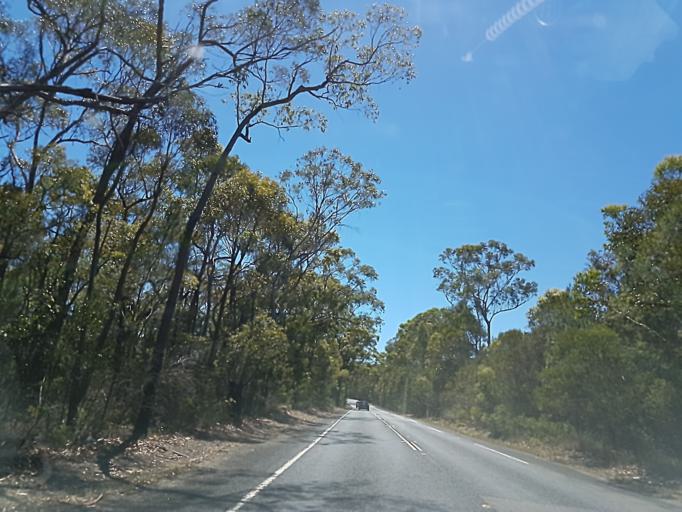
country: AU
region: New South Wales
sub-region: Hornsby Shire
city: Glenorie
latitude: -33.5253
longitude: 151.0210
